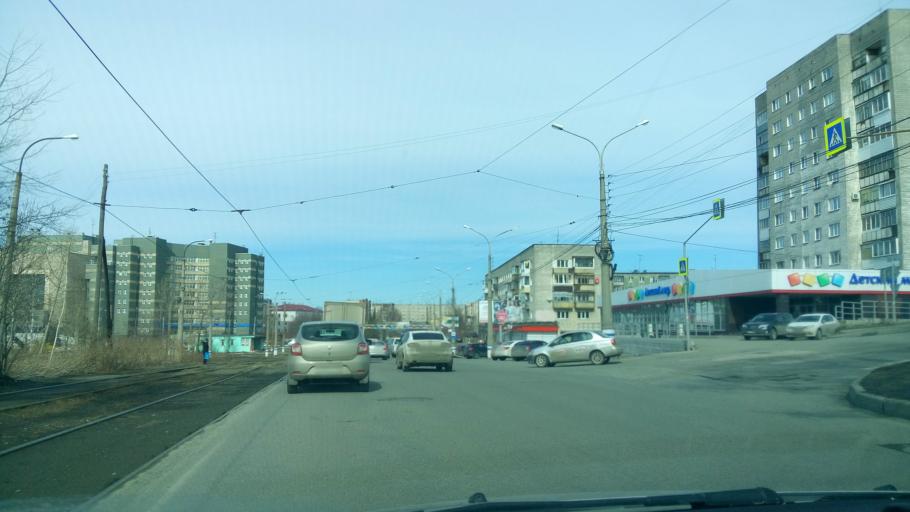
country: RU
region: Sverdlovsk
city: Nizhniy Tagil
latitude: 57.9070
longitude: 59.9489
